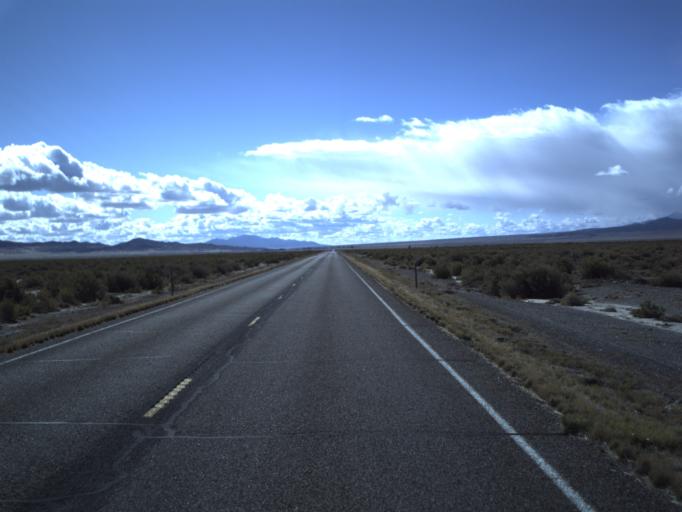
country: US
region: Nevada
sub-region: White Pine County
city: McGill
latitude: 39.0487
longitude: -114.0364
